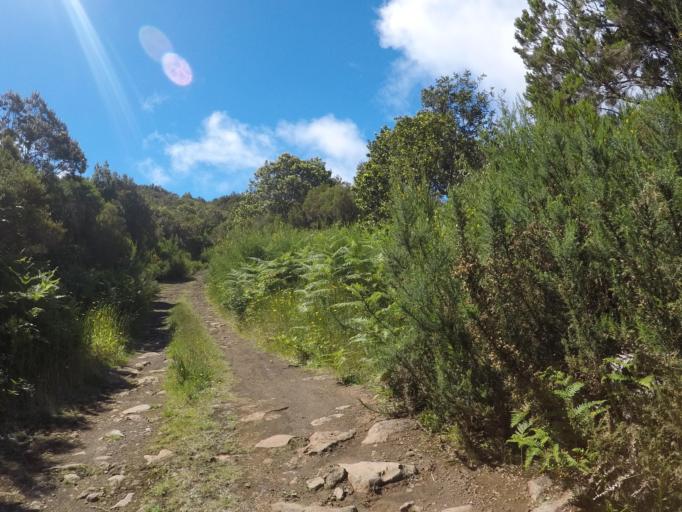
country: PT
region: Madeira
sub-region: Sao Vicente
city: Sao Vicente
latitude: 32.7695
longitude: -17.0588
